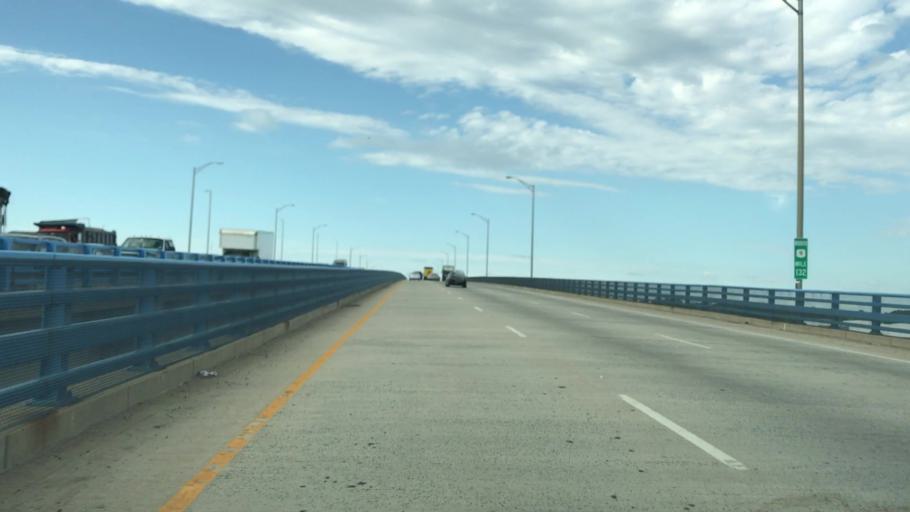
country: US
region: New Jersey
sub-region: Middlesex County
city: Fords
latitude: 40.5057
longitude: -74.3005
